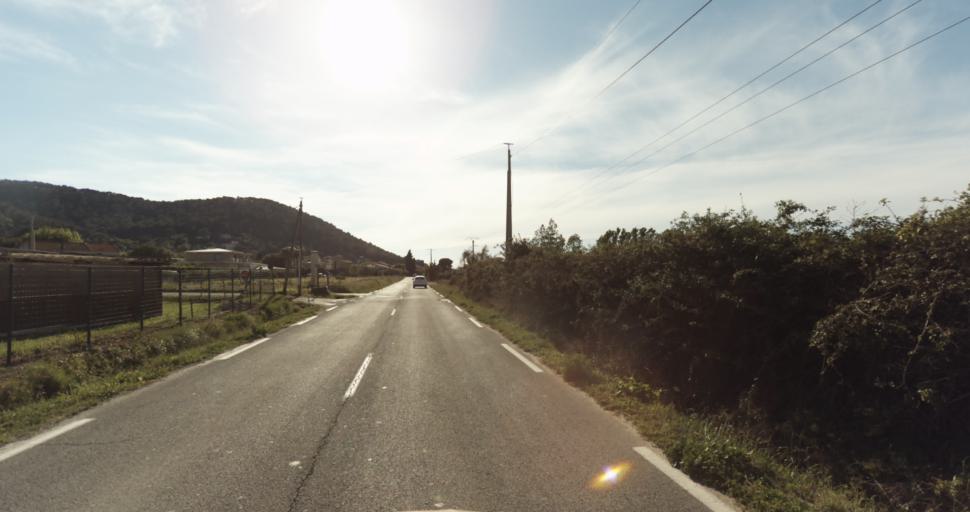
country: FR
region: Provence-Alpes-Cote d'Azur
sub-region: Departement du Var
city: Carqueiranne
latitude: 43.1174
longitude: 6.0844
